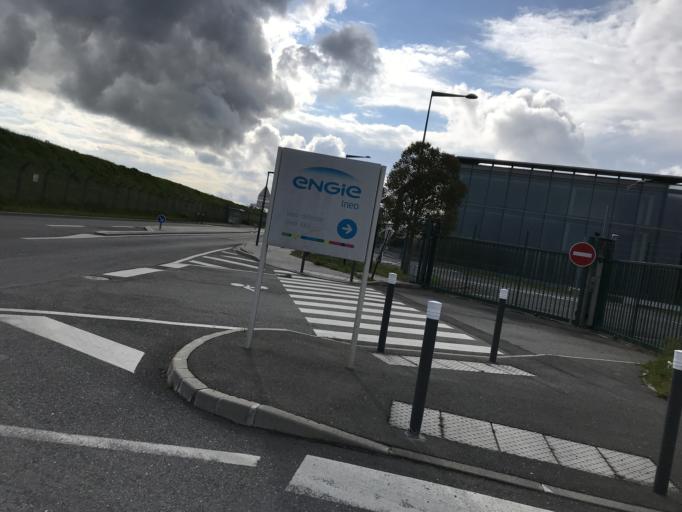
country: FR
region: Ile-de-France
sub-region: Departement des Yvelines
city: Velizy-Villacoublay
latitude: 48.7775
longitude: 2.1953
